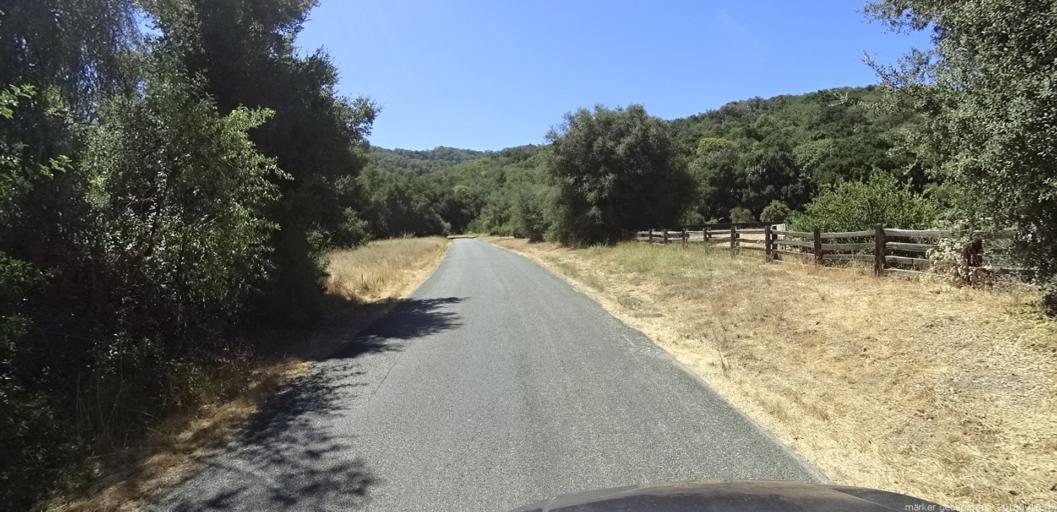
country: US
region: California
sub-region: Monterey County
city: Carmel Valley Village
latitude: 36.4441
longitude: -121.7958
